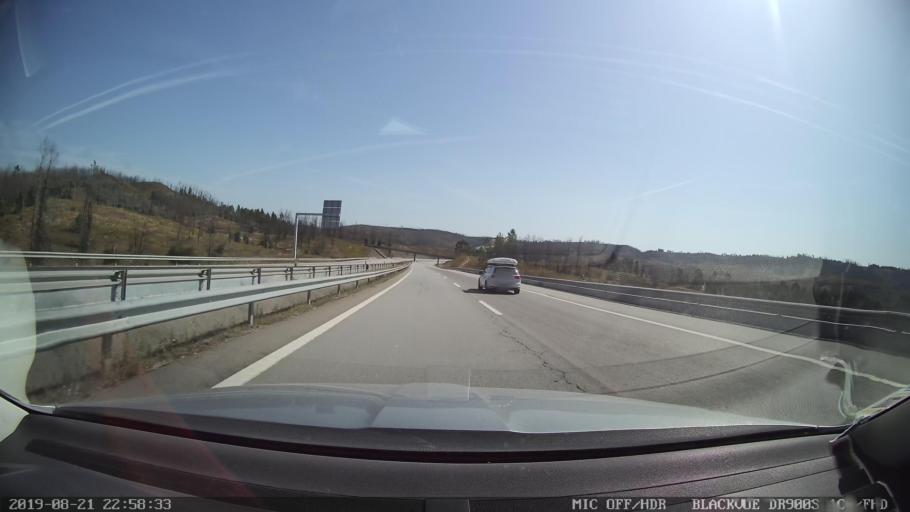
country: PT
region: Santarem
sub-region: Macao
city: Macao
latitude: 39.5198
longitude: -7.9883
